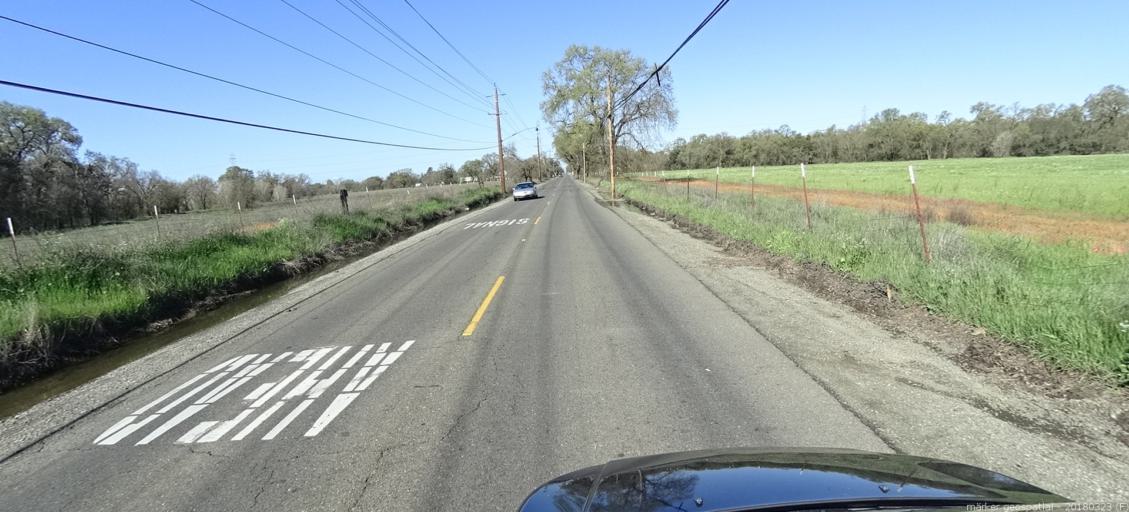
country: US
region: California
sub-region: Sacramento County
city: Rio Linda
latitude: 38.6980
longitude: -121.4248
